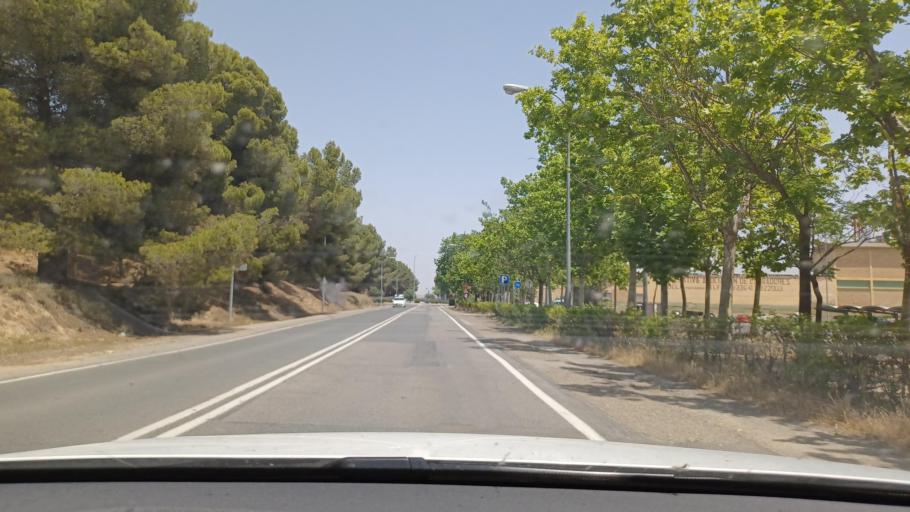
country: ES
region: Navarre
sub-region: Provincia de Navarra
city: Tudela
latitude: 42.0513
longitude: -1.6134
